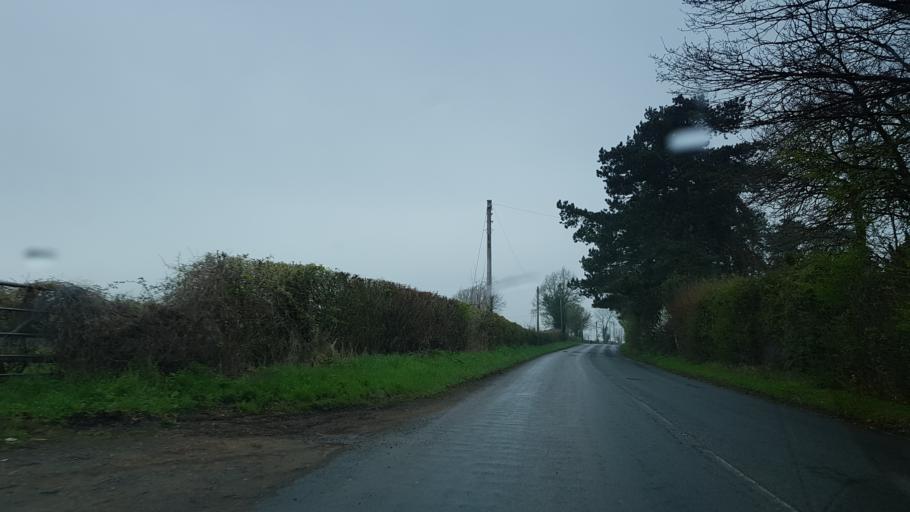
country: GB
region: England
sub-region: Herefordshire
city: Ledbury
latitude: 52.0679
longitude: -2.4493
